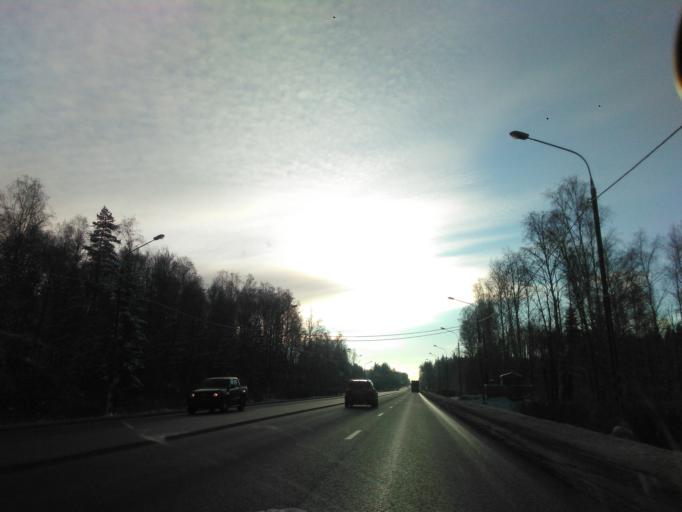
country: RU
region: Moskovskaya
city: Reshetnikovo
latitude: 56.4485
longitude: 36.6042
